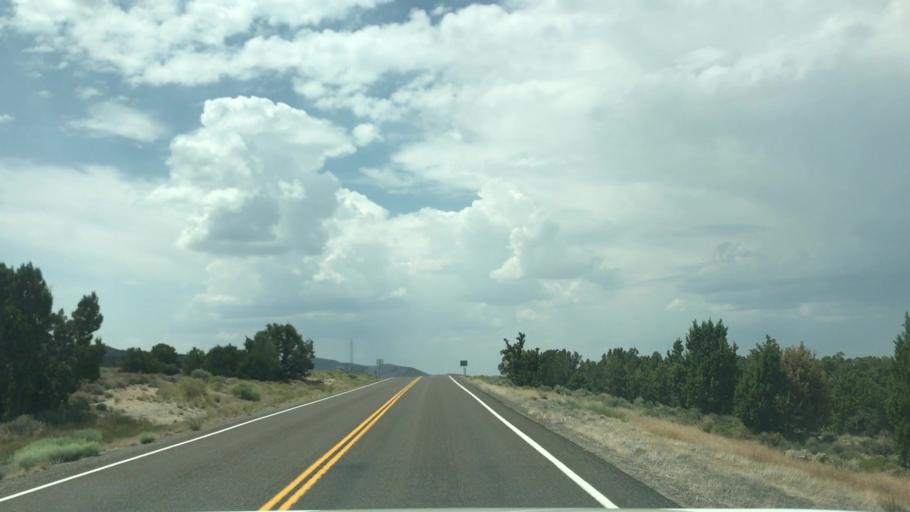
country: US
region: Nevada
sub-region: Eureka County
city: Eureka
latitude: 39.4106
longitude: -115.6953
